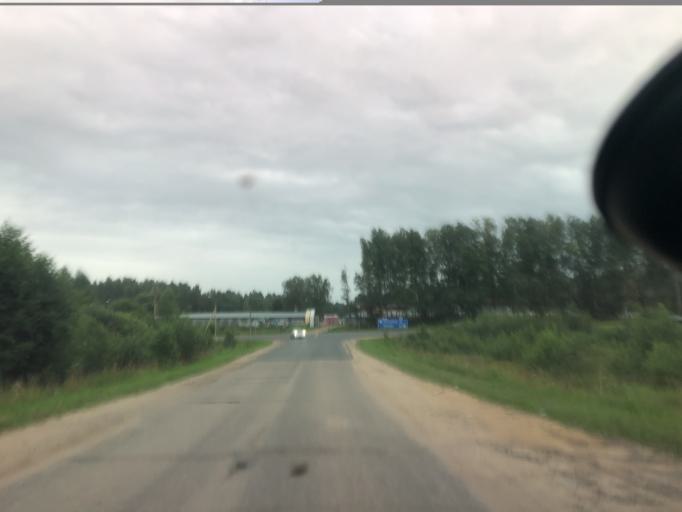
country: RU
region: Jaroslavl
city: Petrovsk
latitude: 56.9834
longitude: 39.2190
